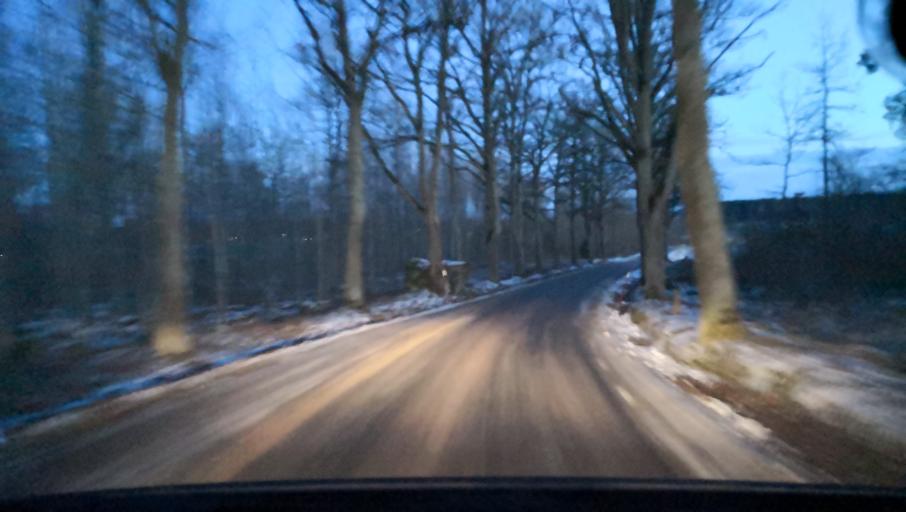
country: SE
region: Soedermanland
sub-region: Katrineholms Kommun
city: Katrineholm
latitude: 59.0711
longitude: 16.3382
